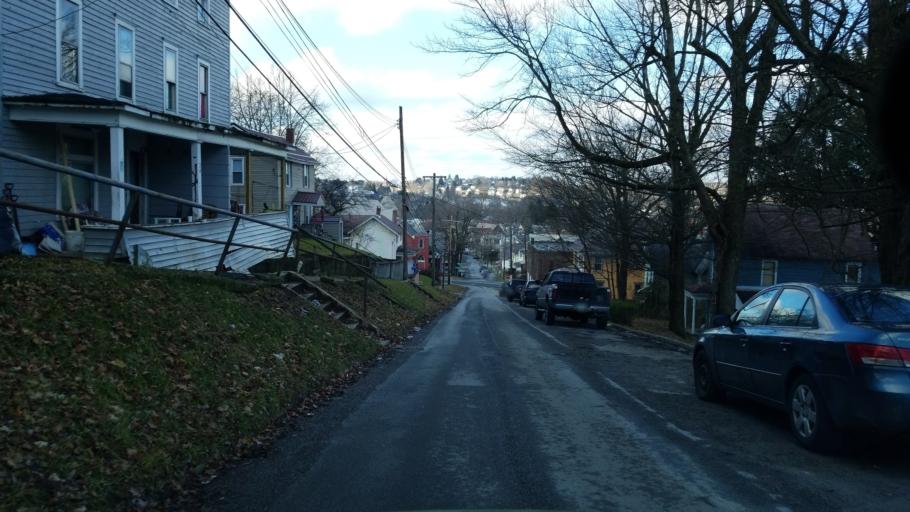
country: US
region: Pennsylvania
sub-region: Clearfield County
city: DuBois
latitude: 41.1163
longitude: -78.7632
